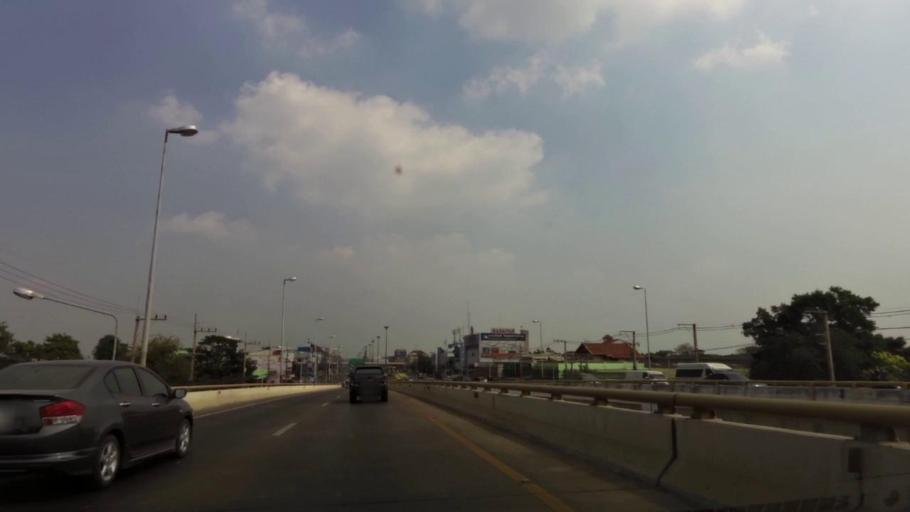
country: TH
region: Phra Nakhon Si Ayutthaya
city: Phra Nakhon Si Ayutthaya
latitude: 14.3527
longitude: 100.5848
